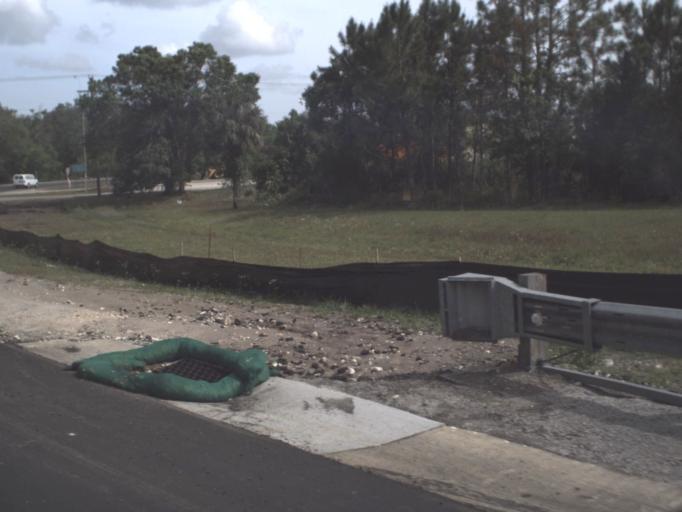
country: US
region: Florida
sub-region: Flagler County
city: Bunnell
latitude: 29.4721
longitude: -81.2645
